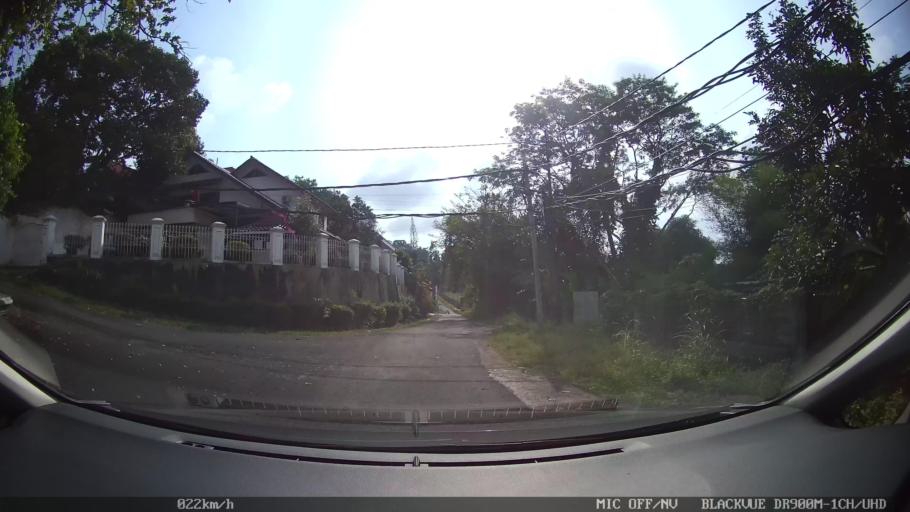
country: ID
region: Lampung
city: Bandarlampung
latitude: -5.4282
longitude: 105.2504
